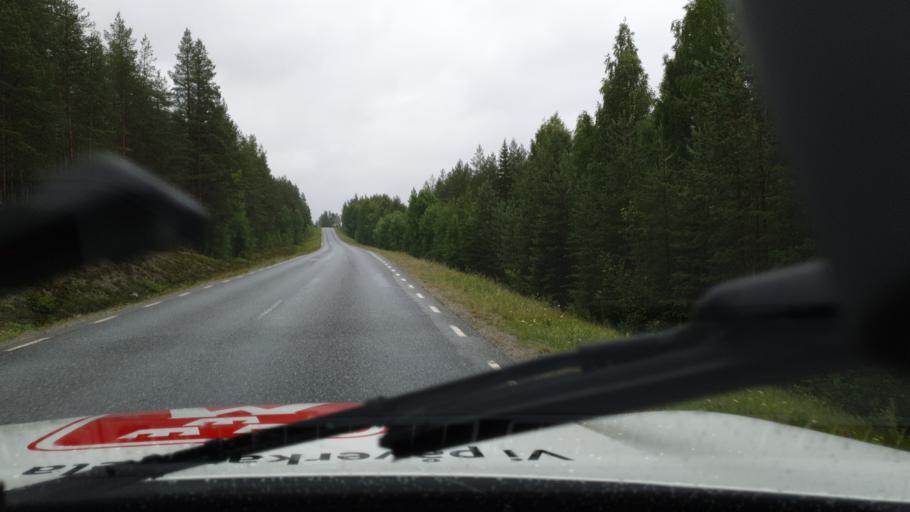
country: SE
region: Vaesterbotten
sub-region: Asele Kommun
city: Asele
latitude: 64.2712
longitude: 17.2750
